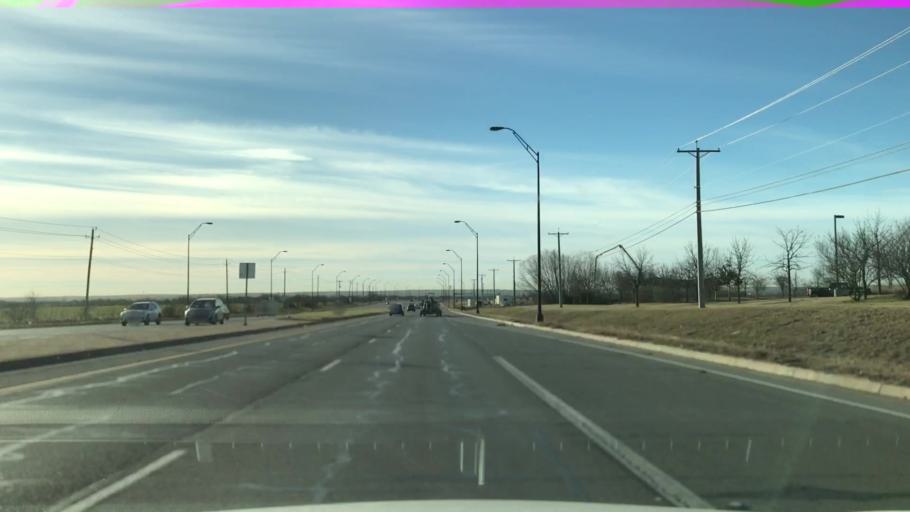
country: US
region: Texas
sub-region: Williamson County
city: Round Rock
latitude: 30.5665
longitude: -97.6483
